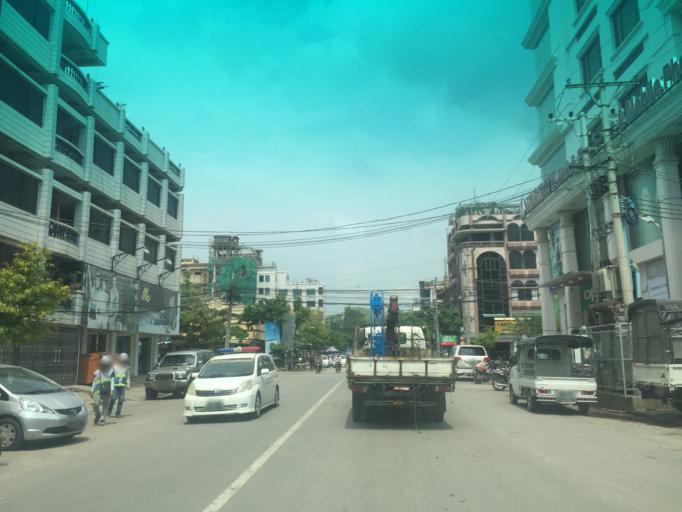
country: MM
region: Mandalay
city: Mandalay
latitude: 21.9802
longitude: 96.0838
